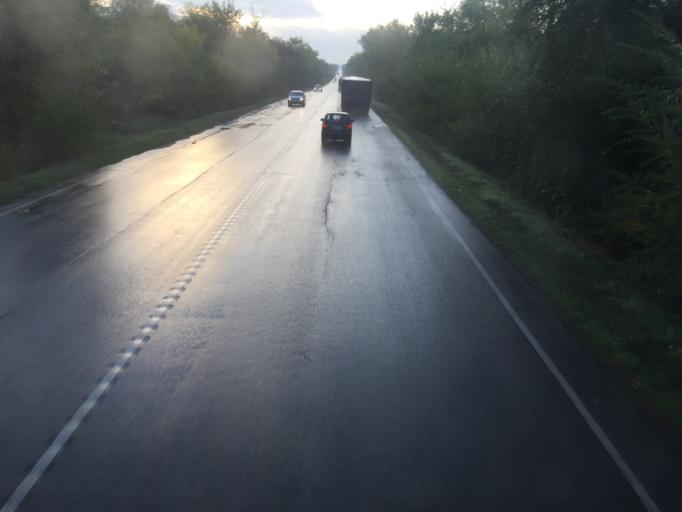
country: RU
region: Rostov
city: Bataysk
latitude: 47.0381
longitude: 39.8634
